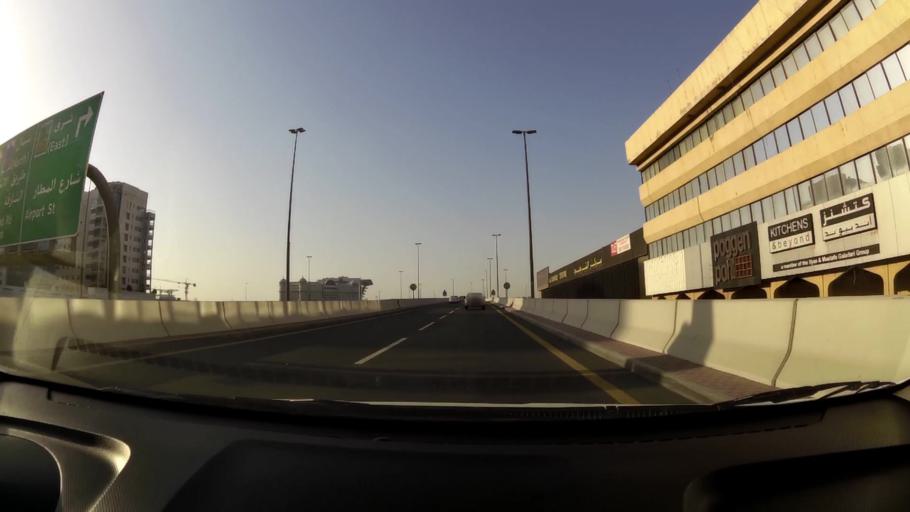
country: AE
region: Ash Shariqah
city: Sharjah
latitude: 25.2538
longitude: 55.3370
